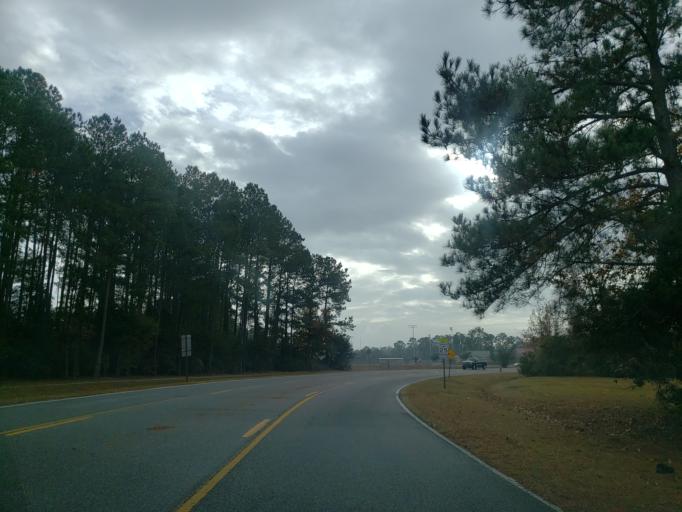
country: US
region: Georgia
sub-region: Chatham County
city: Whitemarsh Island
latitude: 32.0399
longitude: -81.0088
